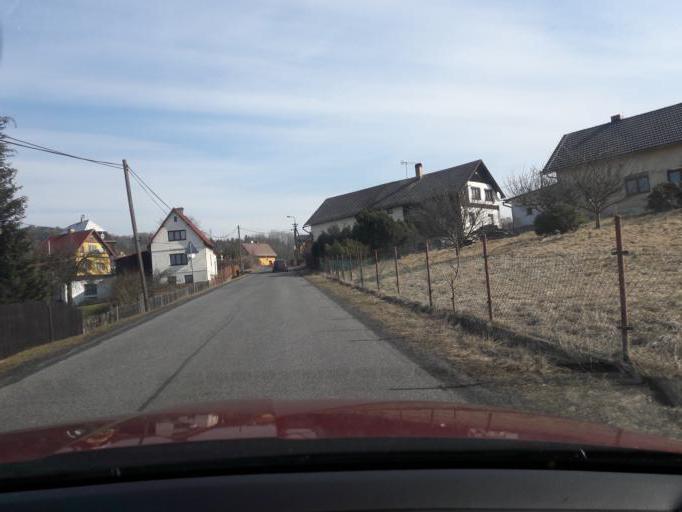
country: CZ
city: Novy Bor
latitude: 50.7670
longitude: 14.5285
